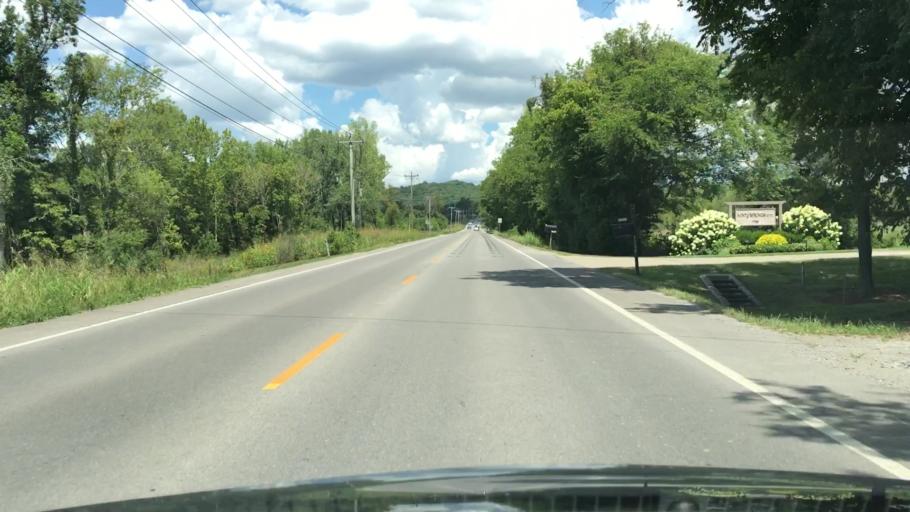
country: US
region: Tennessee
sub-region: Williamson County
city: Nolensville
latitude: 35.8882
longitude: -86.6641
